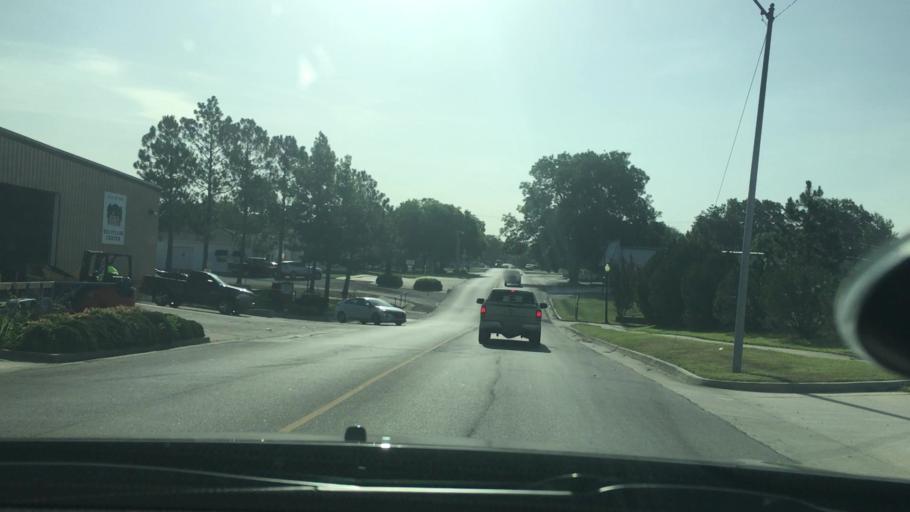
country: US
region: Oklahoma
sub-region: Pontotoc County
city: Ada
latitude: 34.7734
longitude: -96.6745
